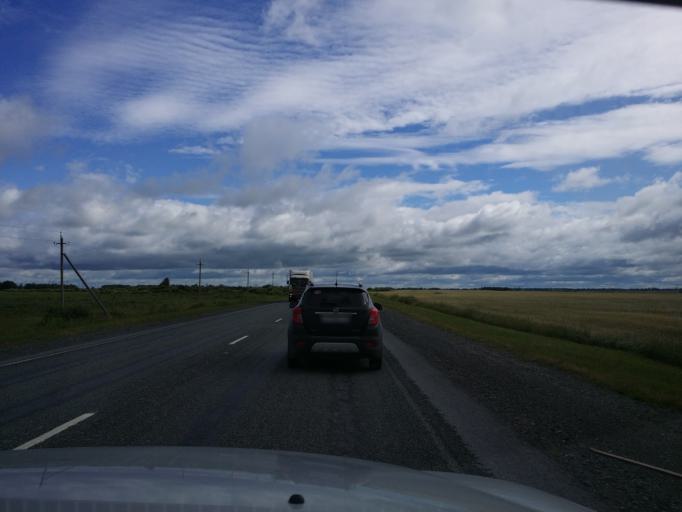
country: RU
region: Tjumen
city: Yarkovo
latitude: 57.2857
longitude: 66.8900
